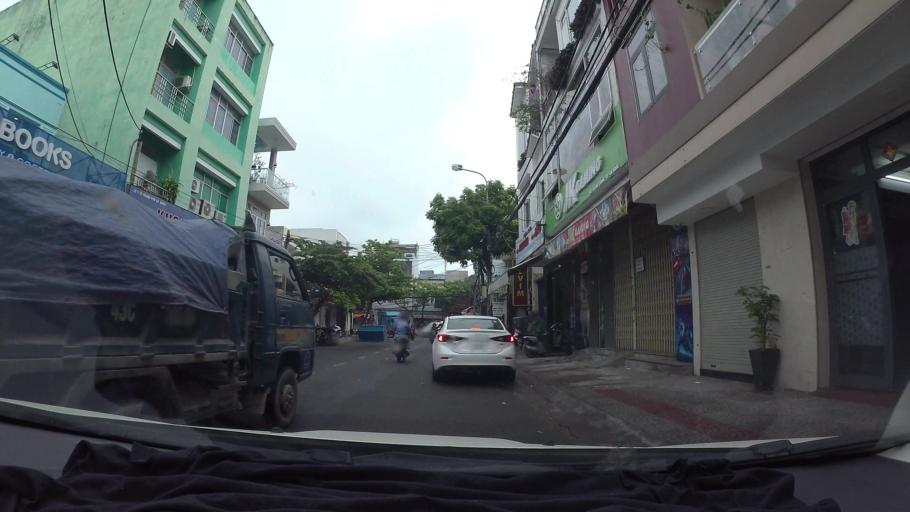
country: VN
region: Da Nang
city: Da Nang
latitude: 16.0759
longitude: 108.2145
